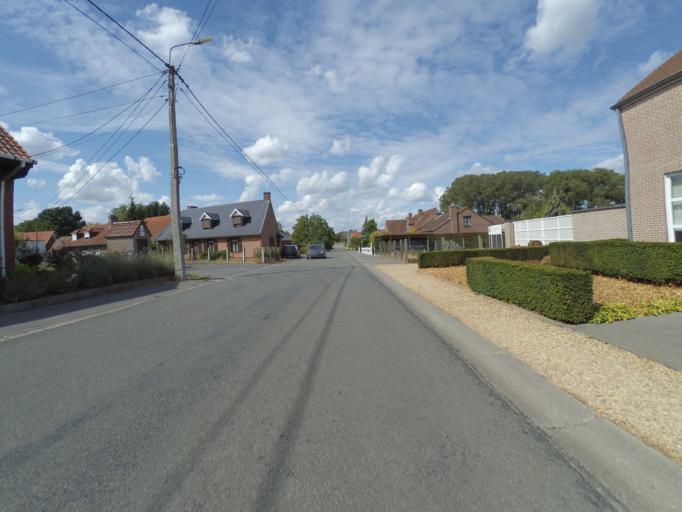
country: BE
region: Flanders
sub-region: Provincie Oost-Vlaanderen
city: Ronse
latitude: 50.7307
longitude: 3.5986
